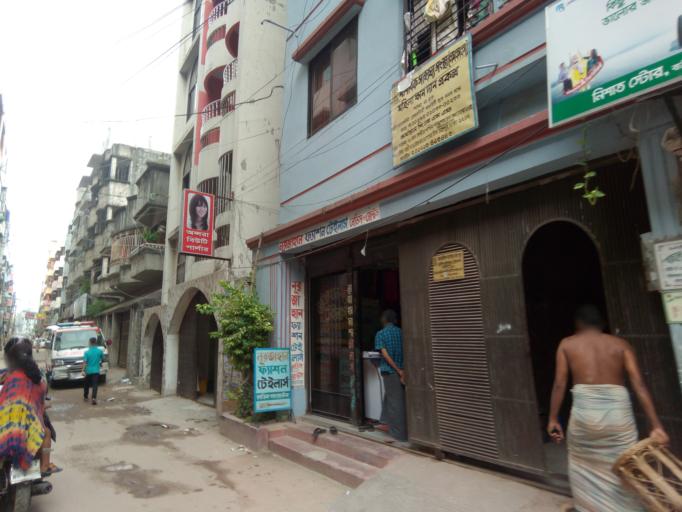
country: BD
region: Dhaka
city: Azimpur
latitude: 23.7659
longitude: 90.3561
